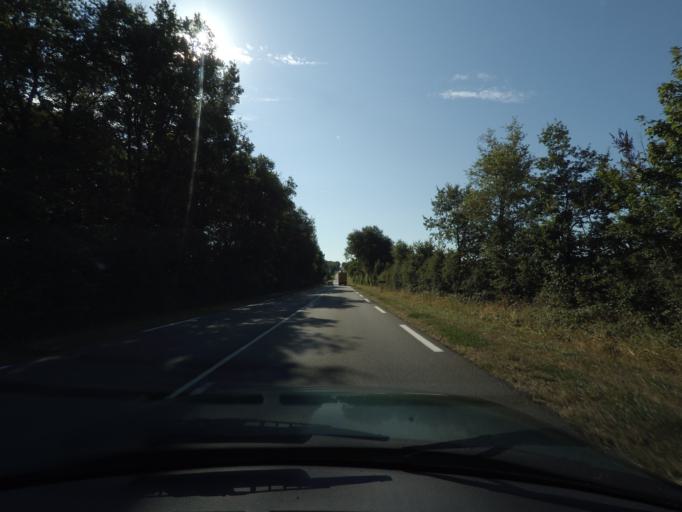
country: FR
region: Poitou-Charentes
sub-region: Departement de la Vienne
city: Terce
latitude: 46.4484
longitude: 0.5721
